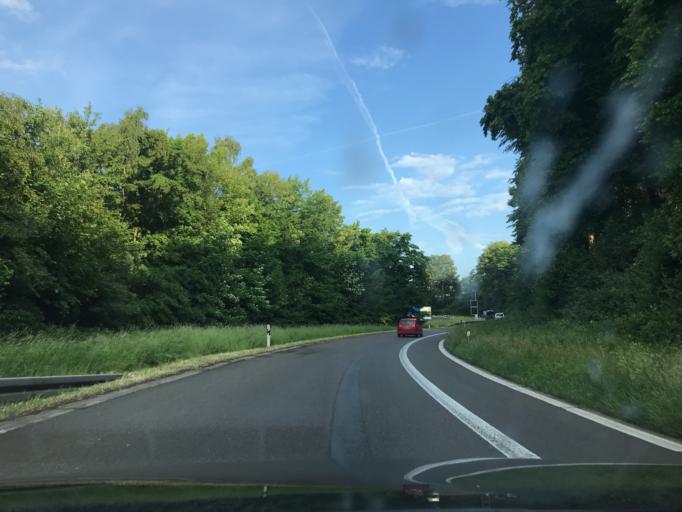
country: DE
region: North Rhine-Westphalia
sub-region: Regierungsbezirk Arnsberg
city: Bochum
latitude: 51.4972
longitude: 7.2740
